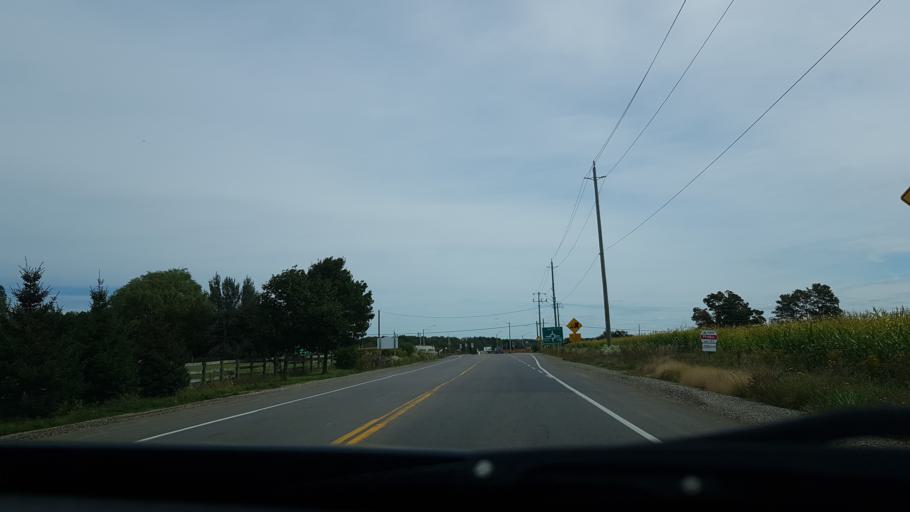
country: CA
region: Ontario
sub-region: Wellington County
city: Guelph
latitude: 43.4719
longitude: -80.3085
